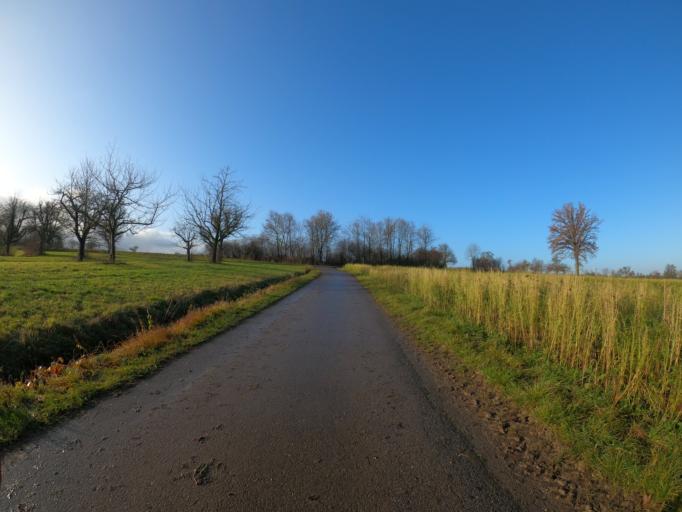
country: DE
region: Baden-Wuerttemberg
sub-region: Regierungsbezirk Stuttgart
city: Boll
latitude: 48.6594
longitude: 9.6217
